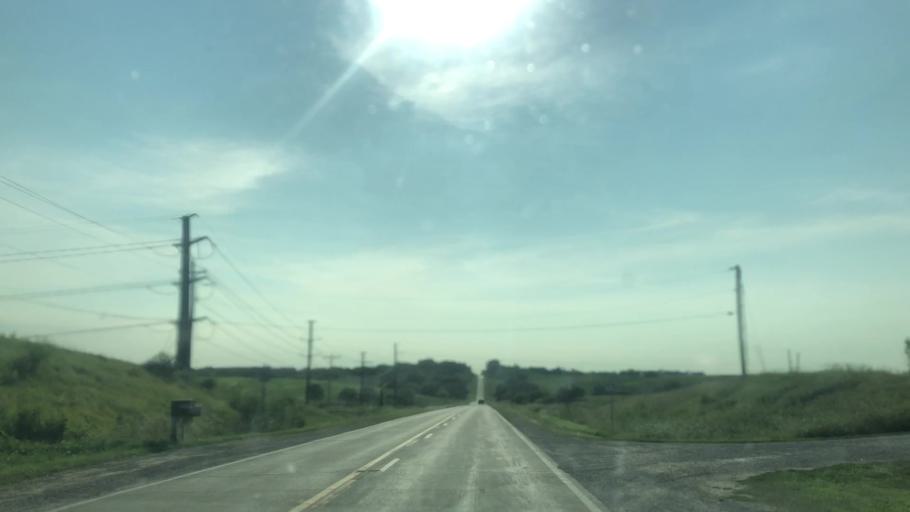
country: US
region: Iowa
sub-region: Marshall County
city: Marshalltown
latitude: 42.0489
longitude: -92.9628
